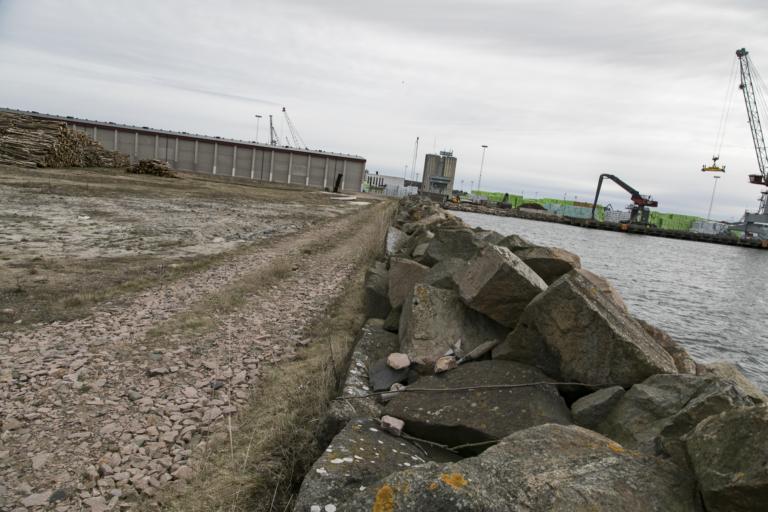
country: SE
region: Halland
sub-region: Varbergs Kommun
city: Varberg
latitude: 57.1176
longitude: 12.2377
